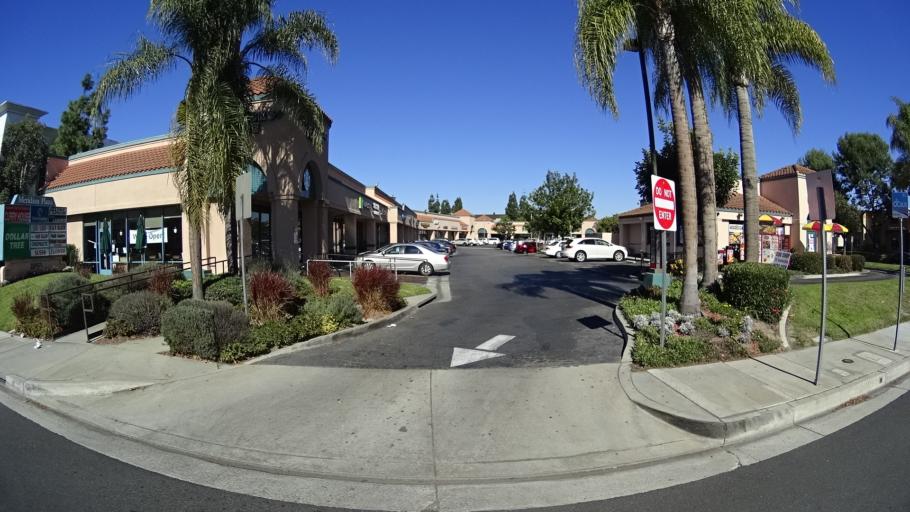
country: US
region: California
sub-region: Orange County
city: Stanton
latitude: 33.8030
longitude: -118.0147
